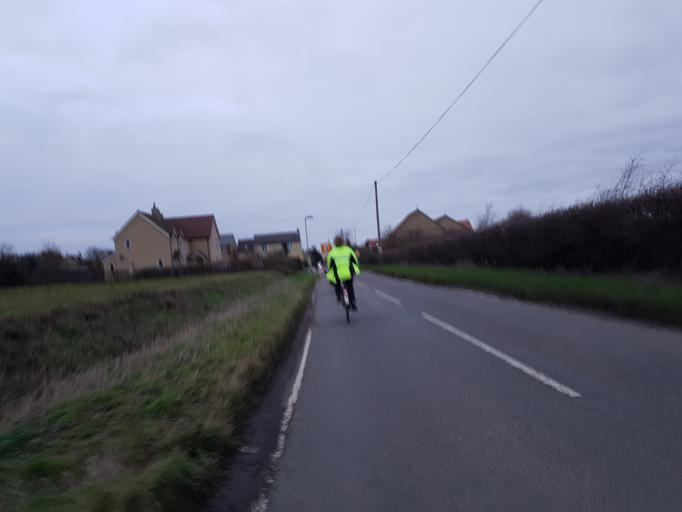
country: GB
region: England
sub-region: Cambridgeshire
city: Waterbeach
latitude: 52.2188
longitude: 0.1793
